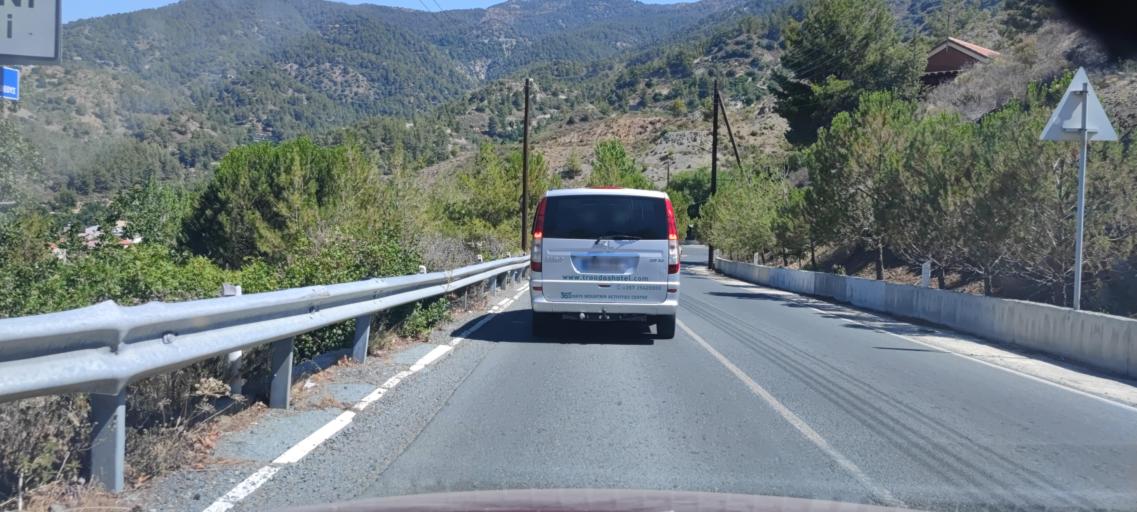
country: CY
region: Lefkosia
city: Kakopetria
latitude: 34.8892
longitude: 32.8389
